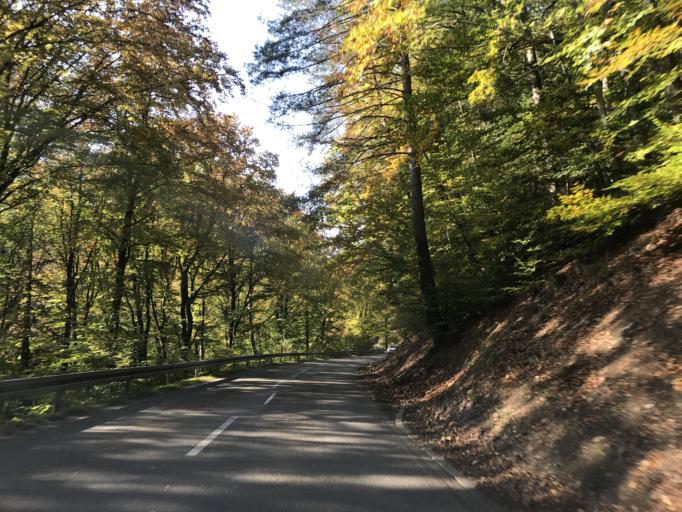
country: DE
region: Baden-Wuerttemberg
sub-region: Freiburg Region
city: Gorwihl
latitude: 47.6373
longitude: 8.0701
